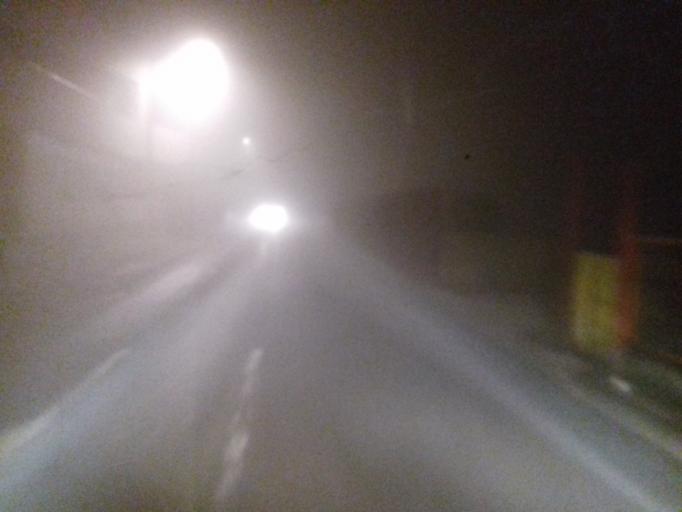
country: BA
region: Federation of Bosnia and Herzegovina
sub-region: Kanton Sarajevo
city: Sarajevo
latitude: 43.8336
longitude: 18.3123
